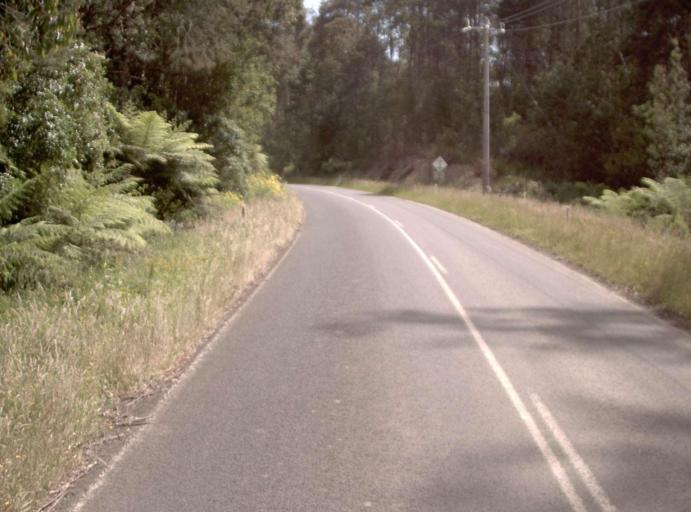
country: AU
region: Victoria
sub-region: Latrobe
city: Moe
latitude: -37.8720
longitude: 146.3771
